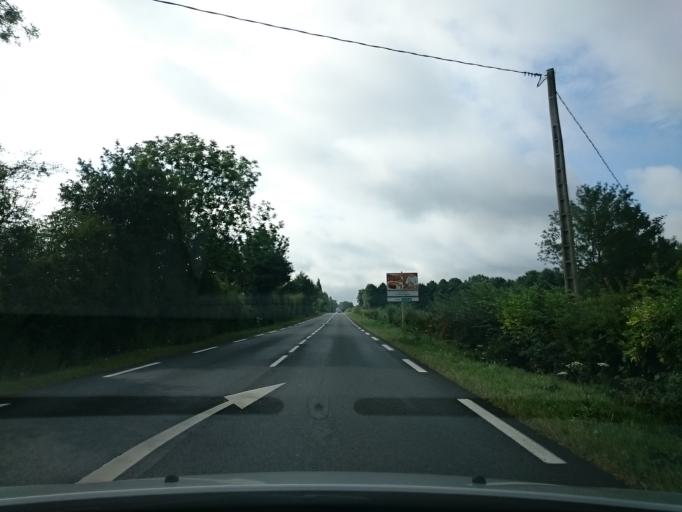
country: FR
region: Lower Normandy
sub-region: Departement du Calvados
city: Cambremer
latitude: 49.1281
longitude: 0.0044
